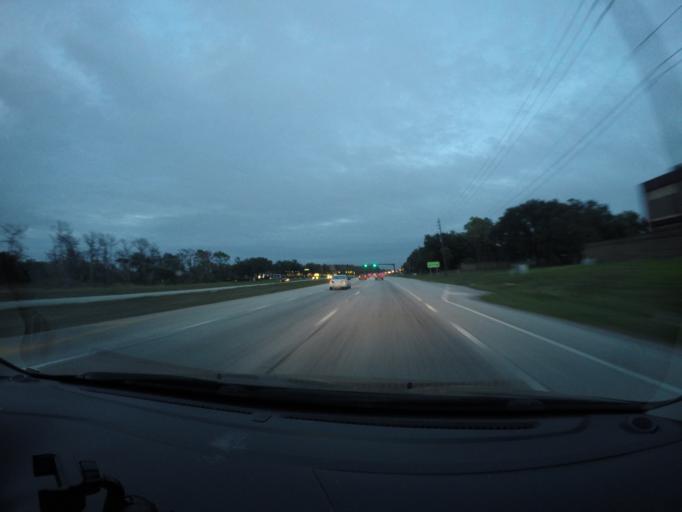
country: US
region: Florida
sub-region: Orange County
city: Tangelo Park
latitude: 28.4499
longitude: -81.4411
